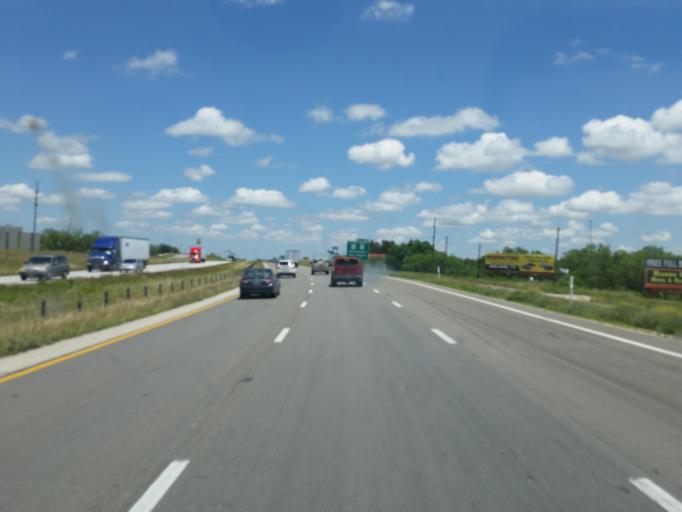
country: US
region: Texas
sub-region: Nolan County
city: Sweetwater
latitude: 32.4475
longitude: -100.4115
